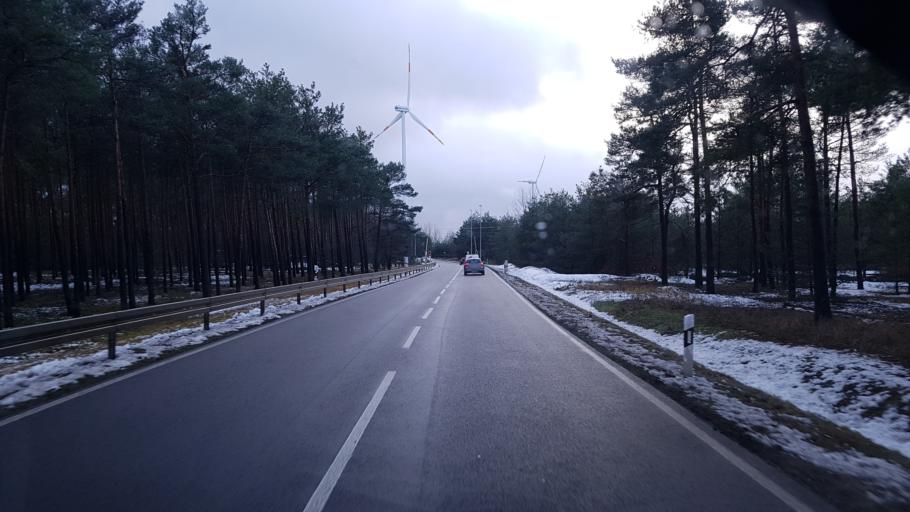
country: DE
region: Brandenburg
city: Heinersbruck
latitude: 51.7762
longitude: 14.4719
